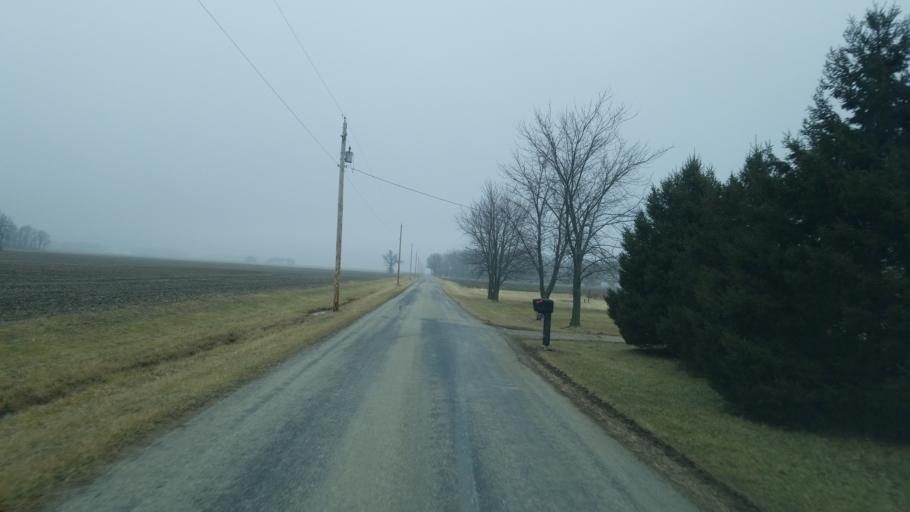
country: US
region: Indiana
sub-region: Adams County
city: Geneva
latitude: 40.5974
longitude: -85.1071
